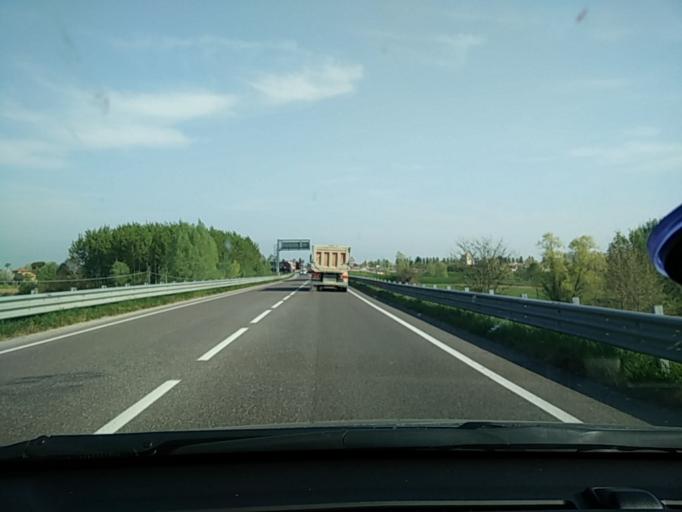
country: IT
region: Veneto
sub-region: Provincia di Treviso
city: Portobuffole
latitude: 45.8477
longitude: 12.5368
